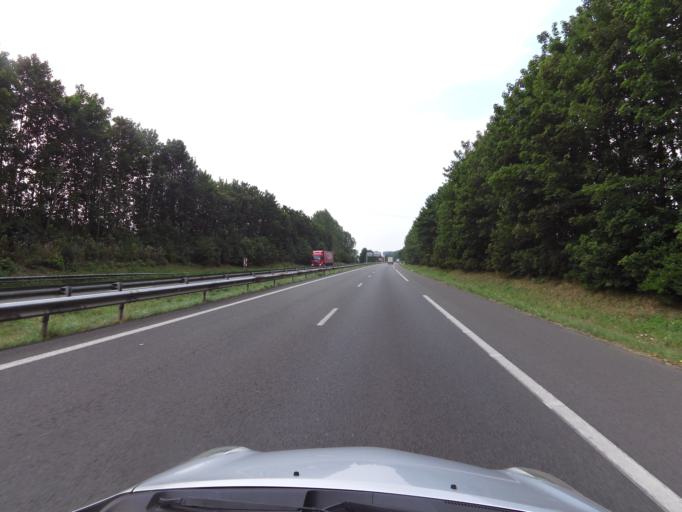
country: FR
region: Nord-Pas-de-Calais
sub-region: Departement du Pas-de-Calais
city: Bourlon
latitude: 50.1506
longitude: 3.1162
